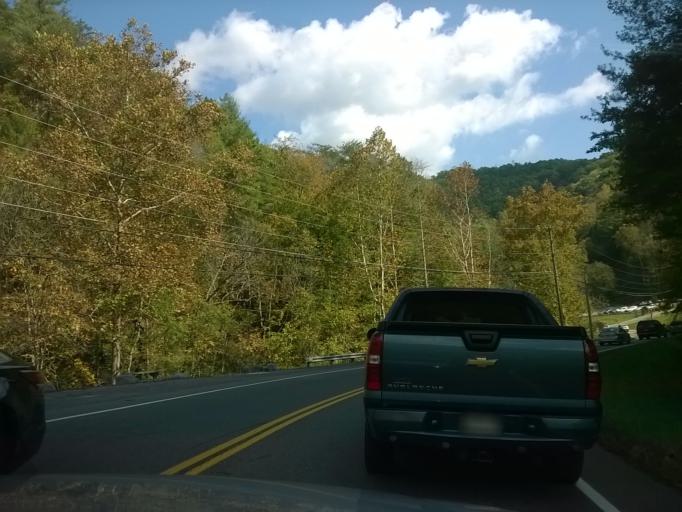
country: US
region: Tennessee
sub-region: Sevier County
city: Pigeon Forge
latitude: 35.7685
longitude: -83.6209
